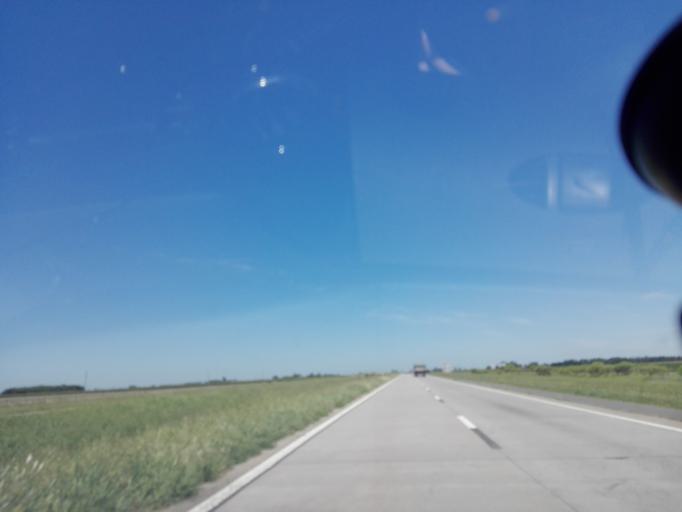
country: AR
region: Santa Fe
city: Armstrong
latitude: -32.8166
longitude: -61.5646
